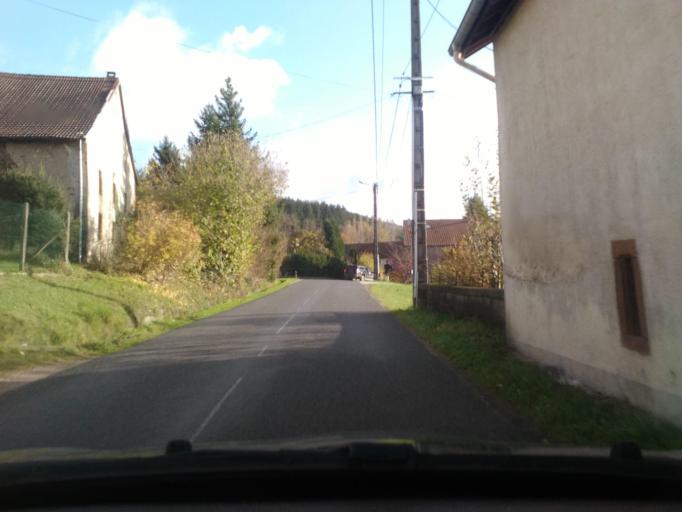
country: FR
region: Lorraine
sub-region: Departement des Vosges
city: Ban-de-Laveline
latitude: 48.2636
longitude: 7.0594
